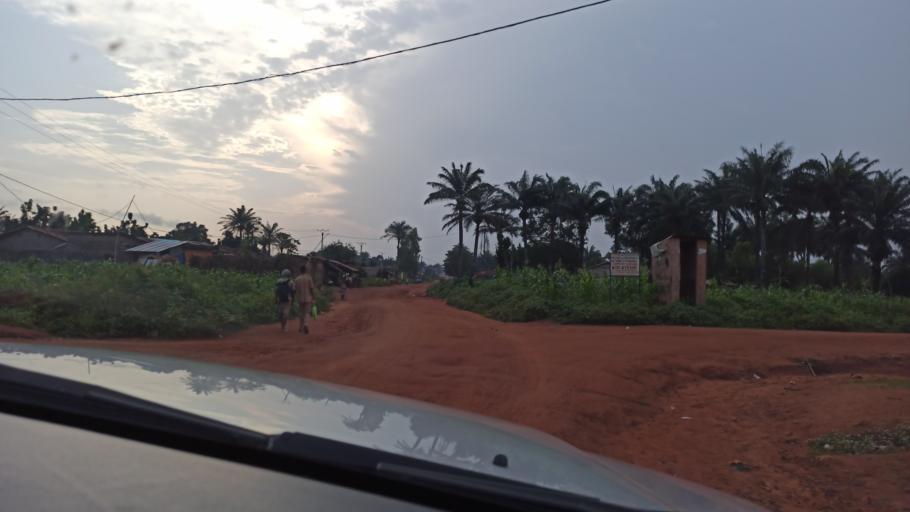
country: BJ
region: Queme
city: Porto-Novo
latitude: 6.5353
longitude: 2.6531
